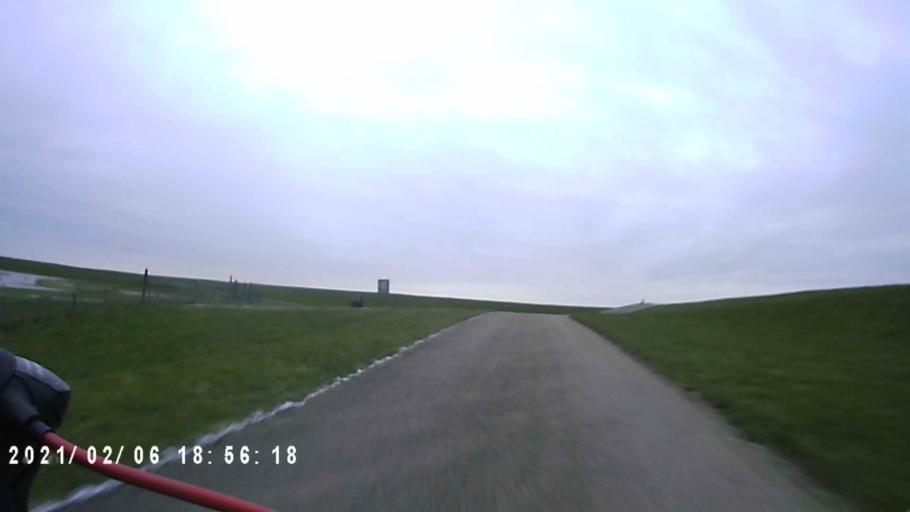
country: NL
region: Groningen
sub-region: Gemeente Winsum
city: Winsum
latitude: 53.4259
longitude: 6.5233
